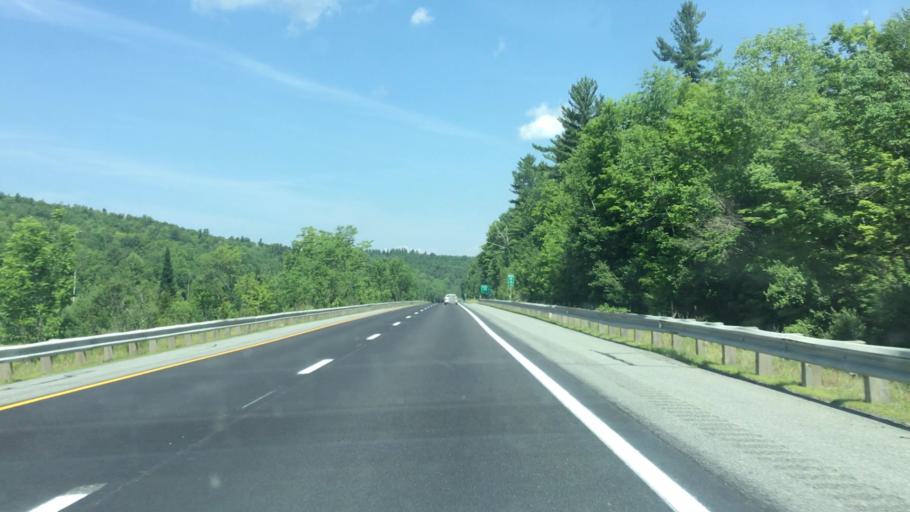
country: US
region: New Hampshire
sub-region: Grafton County
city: Enfield
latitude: 43.5835
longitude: -72.1629
